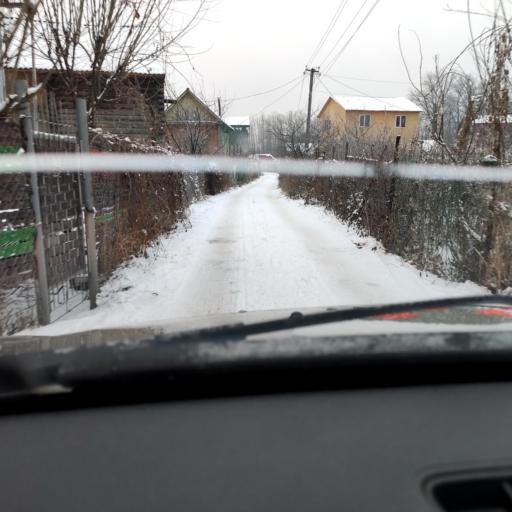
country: RU
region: Bashkortostan
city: Ufa
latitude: 54.6934
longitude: 55.8912
